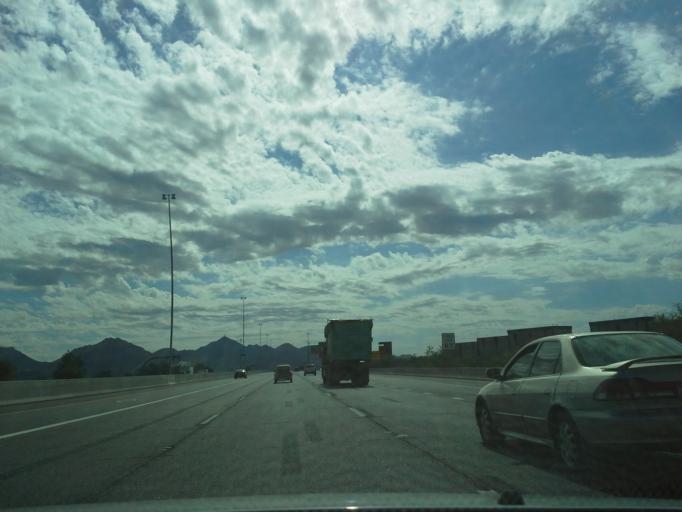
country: US
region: Arizona
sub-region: Maricopa County
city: Paradise Valley
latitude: 33.6599
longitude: -111.9343
